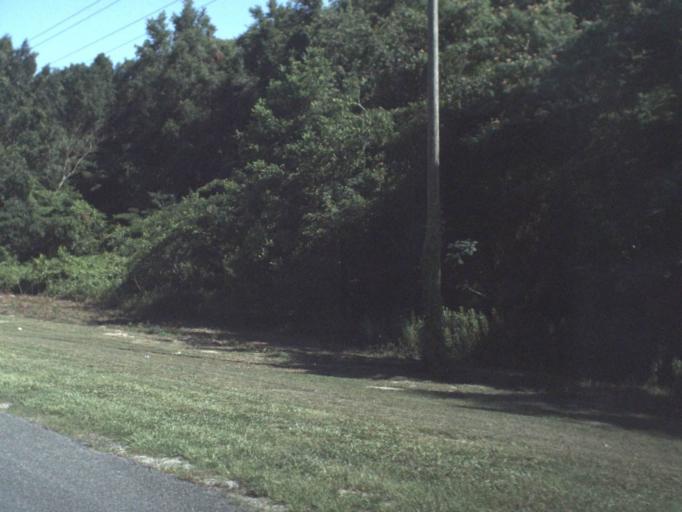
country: US
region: Florida
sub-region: Alachua County
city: High Springs
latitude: 29.9124
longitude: -82.7025
